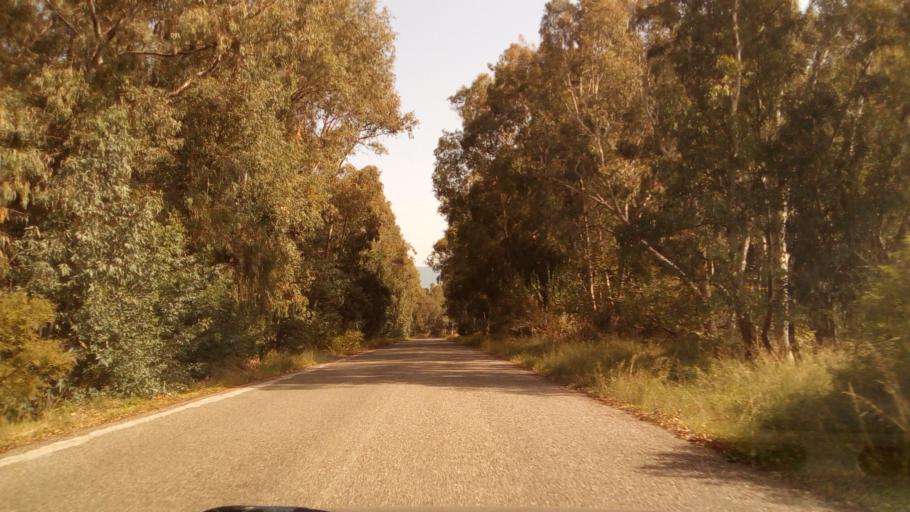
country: GR
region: West Greece
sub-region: Nomos Aitolias kai Akarnanias
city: Nafpaktos
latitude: 38.4008
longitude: 21.8730
